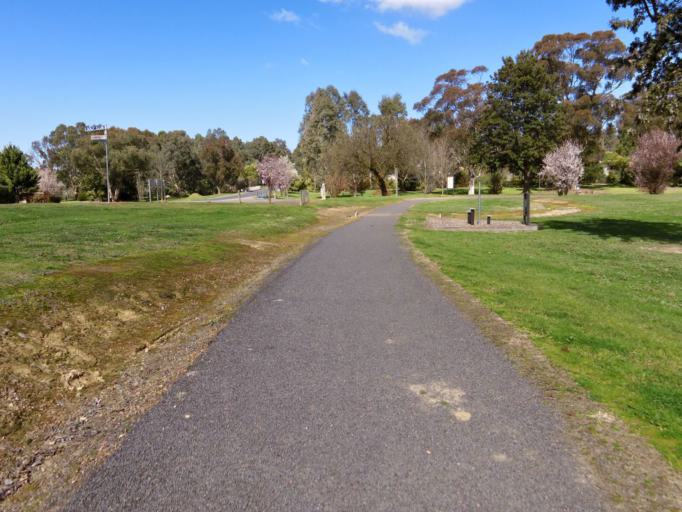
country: AU
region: Victoria
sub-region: Murrindindi
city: Alexandra
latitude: -37.1864
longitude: 145.7149
